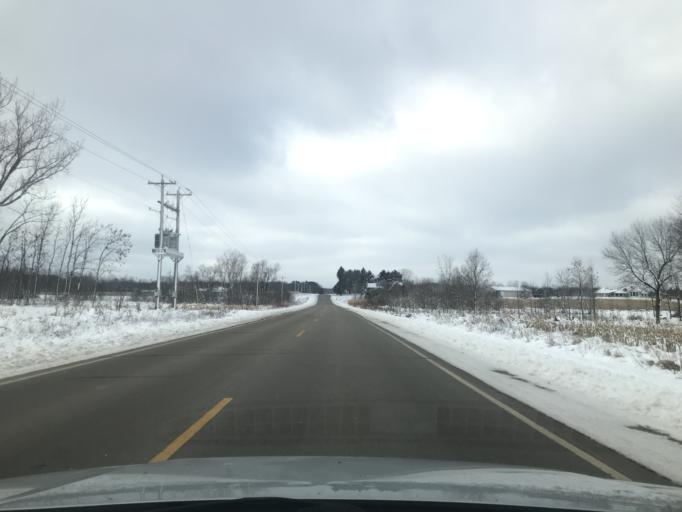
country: US
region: Wisconsin
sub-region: Oconto County
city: Oconto
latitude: 44.9503
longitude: -87.9667
